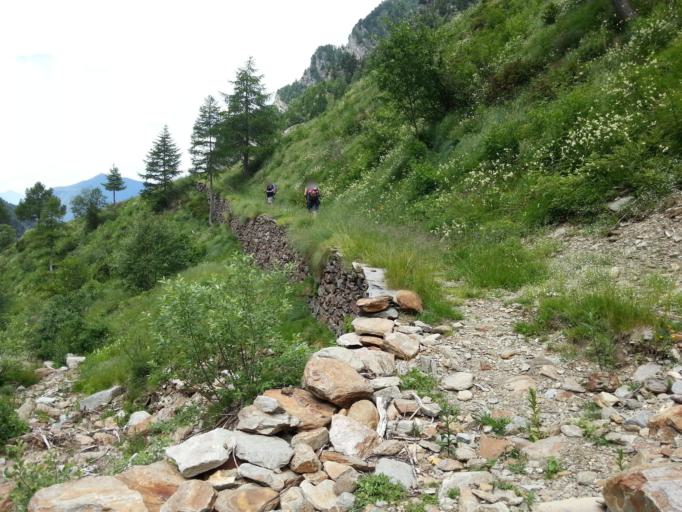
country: IT
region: Lombardy
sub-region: Provincia di Sondrio
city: Gerola Alta
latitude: 46.0555
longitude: 9.4919
